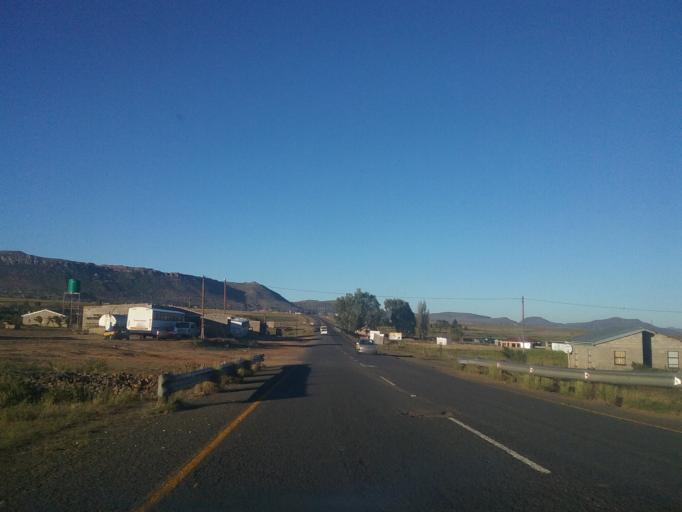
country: LS
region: Mohale's Hoek District
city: Mohale's Hoek
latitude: -30.1546
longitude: 27.4401
